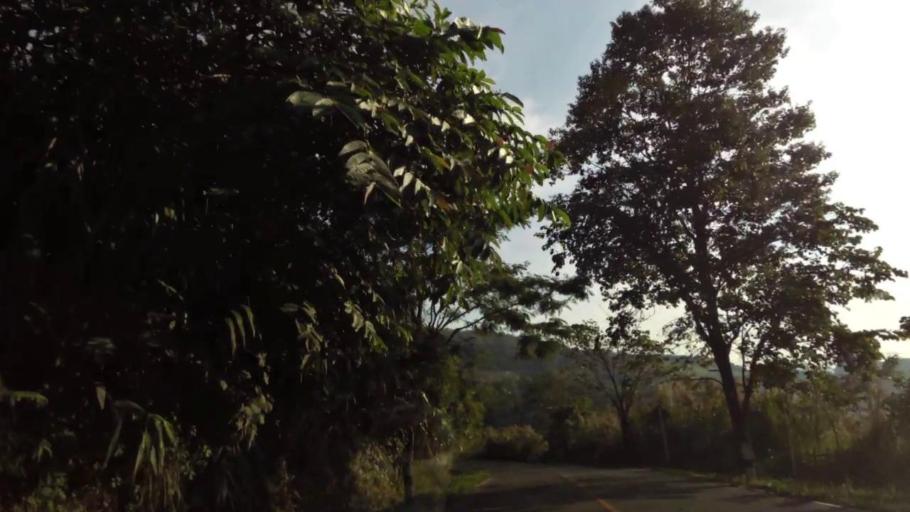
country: TH
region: Chiang Rai
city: Khun Tan
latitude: 19.8491
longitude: 100.4410
